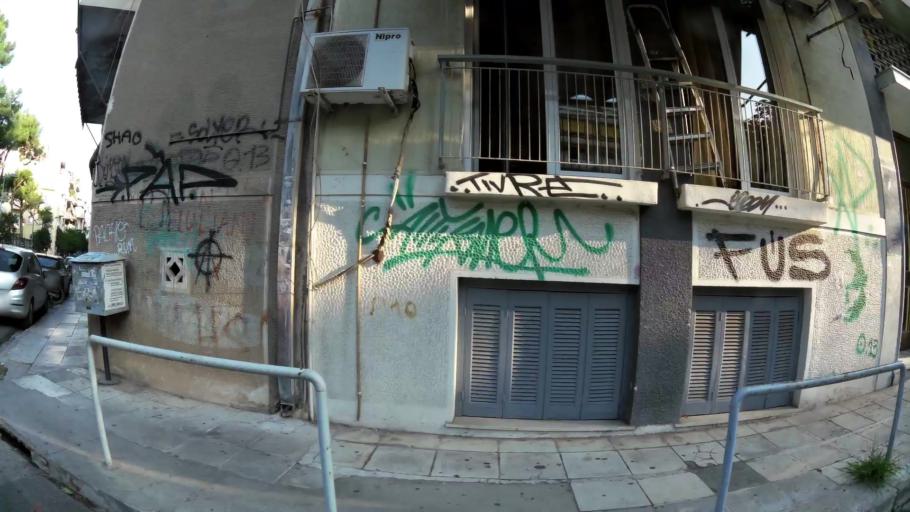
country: GR
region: Attica
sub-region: Nomarchia Athinas
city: Kaisariani
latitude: 37.9775
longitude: 23.7592
